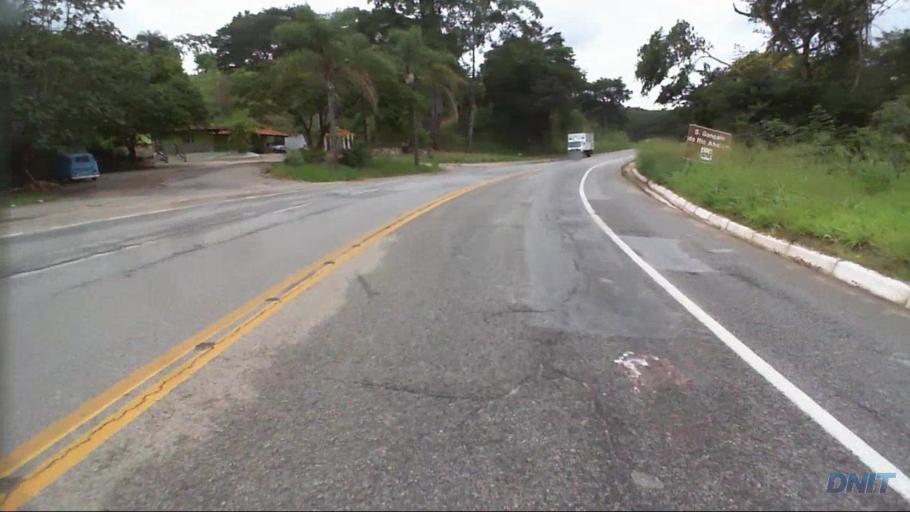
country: BR
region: Minas Gerais
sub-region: Joao Monlevade
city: Joao Monlevade
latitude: -19.8396
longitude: -43.3343
